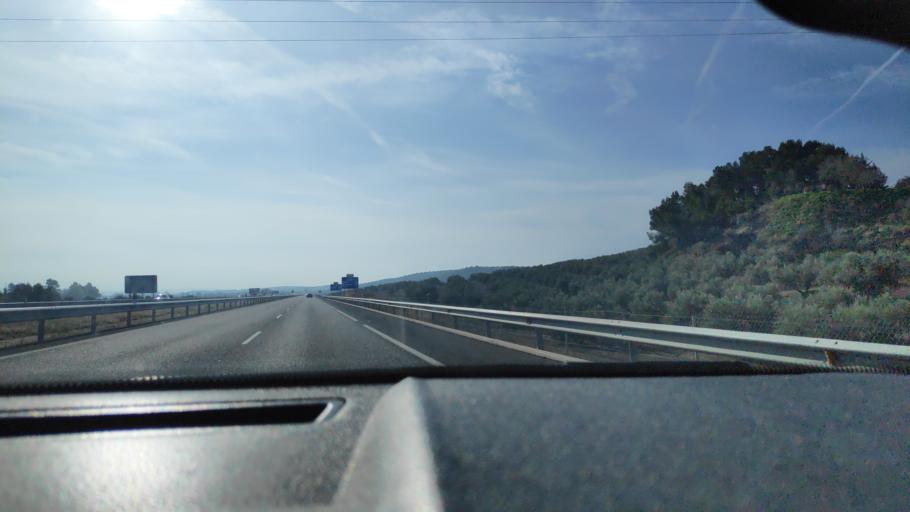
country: ES
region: Andalusia
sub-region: Provincia de Jaen
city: Mengibar
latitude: 37.9009
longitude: -3.7819
